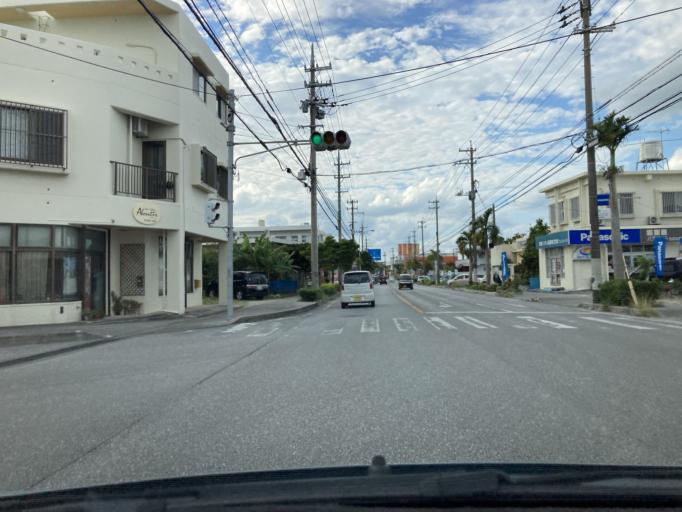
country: JP
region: Okinawa
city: Okinawa
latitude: 26.3587
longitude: 127.8242
